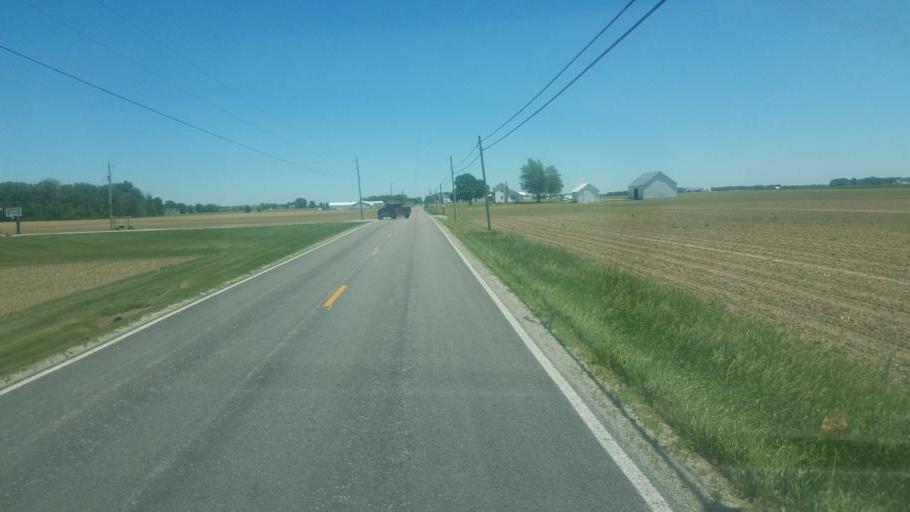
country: US
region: Ohio
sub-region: Darke County
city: Versailles
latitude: 40.2264
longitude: -84.4298
